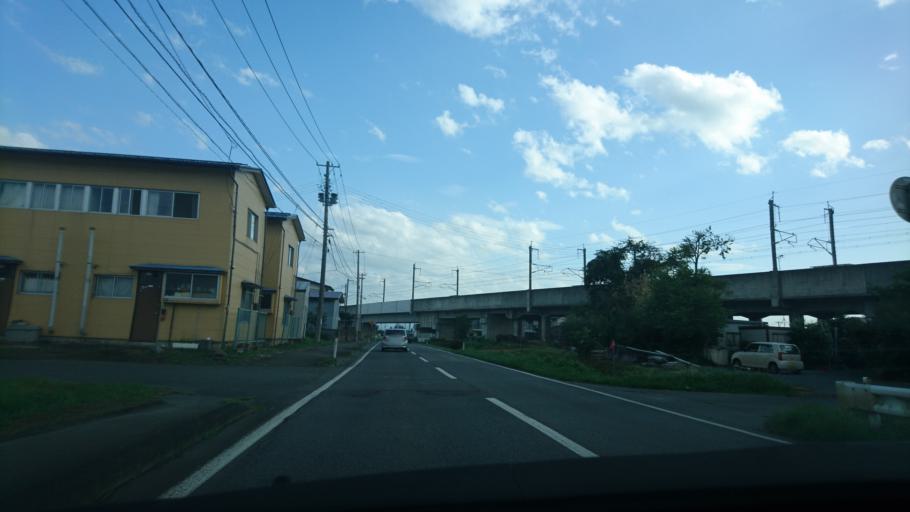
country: JP
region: Iwate
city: Mizusawa
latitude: 39.1742
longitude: 141.1775
